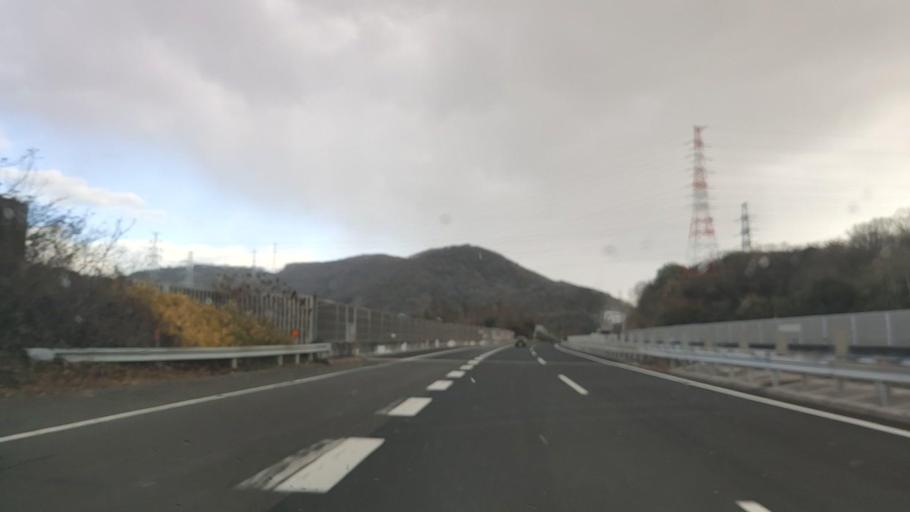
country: JP
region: Okayama
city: Kasaoka
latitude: 34.5358
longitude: 133.5156
